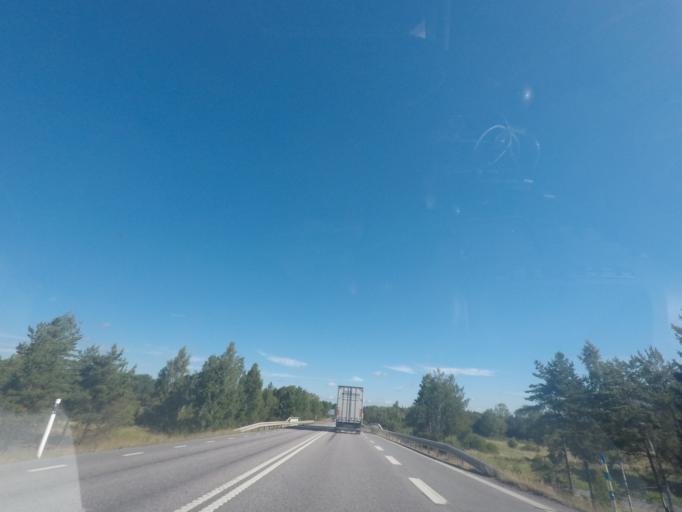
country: SE
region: Soedermanland
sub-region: Strangnas Kommun
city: Strangnas
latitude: 59.3824
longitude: 16.9857
